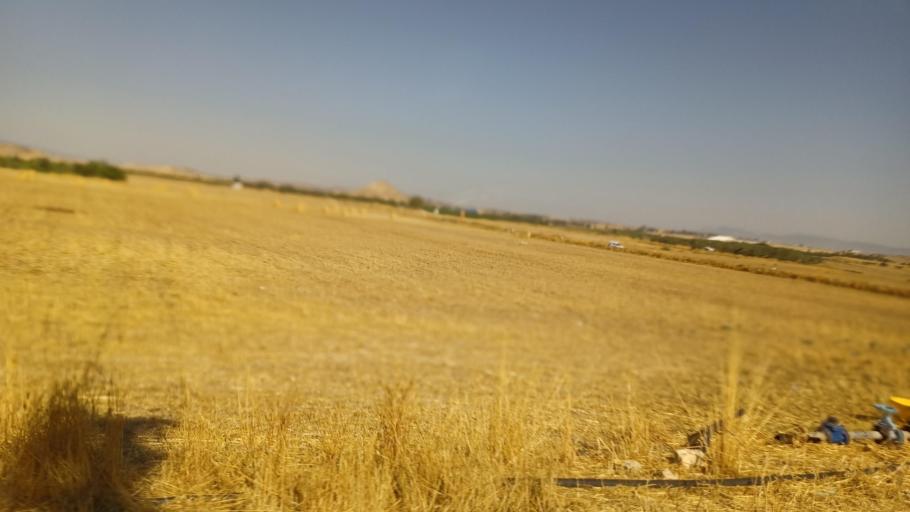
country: CY
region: Larnaka
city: Athienou
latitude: 35.0568
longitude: 33.5191
